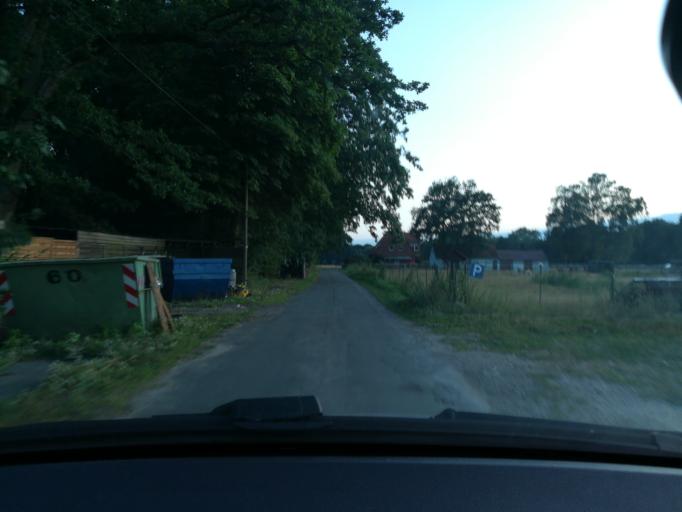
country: DE
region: North Rhine-Westphalia
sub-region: Regierungsbezirk Munster
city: Lienen
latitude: 52.1349
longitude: 7.9890
